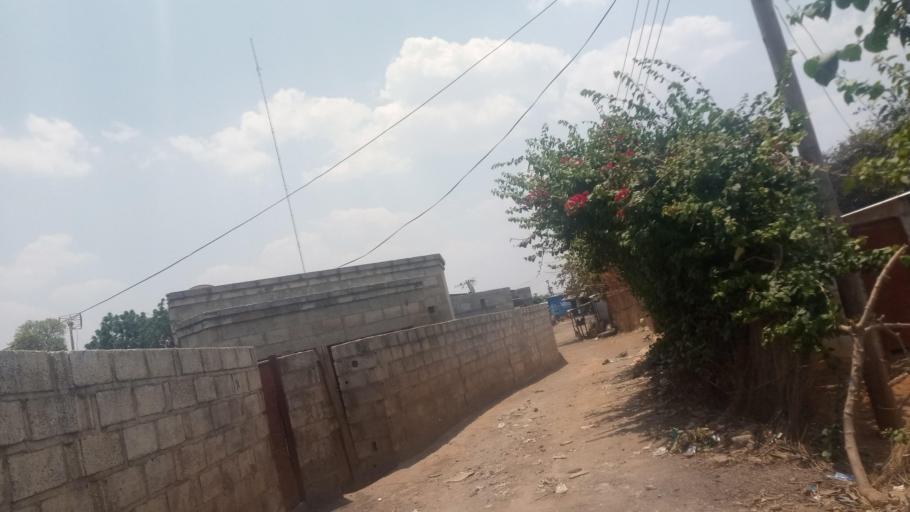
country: ZM
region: Lusaka
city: Lusaka
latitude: -15.4478
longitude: 28.3749
